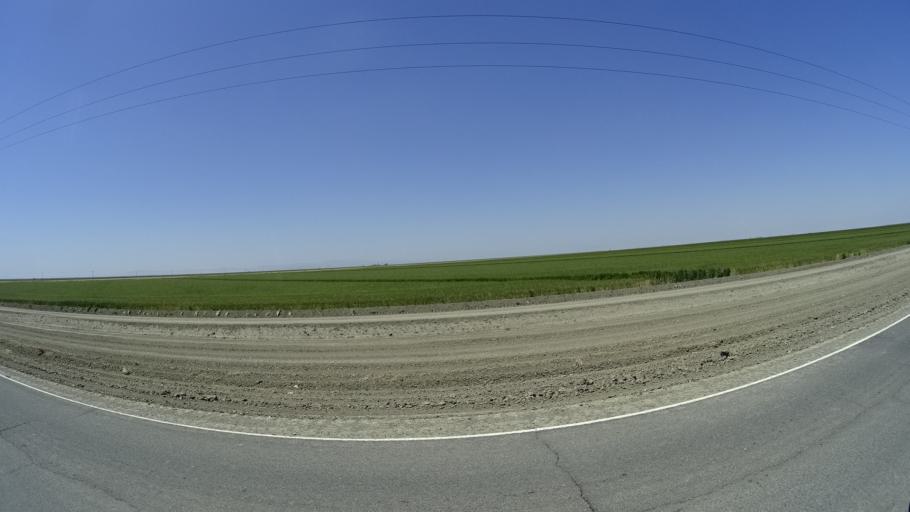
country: US
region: California
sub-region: Kings County
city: Corcoran
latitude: 36.0837
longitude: -119.6440
